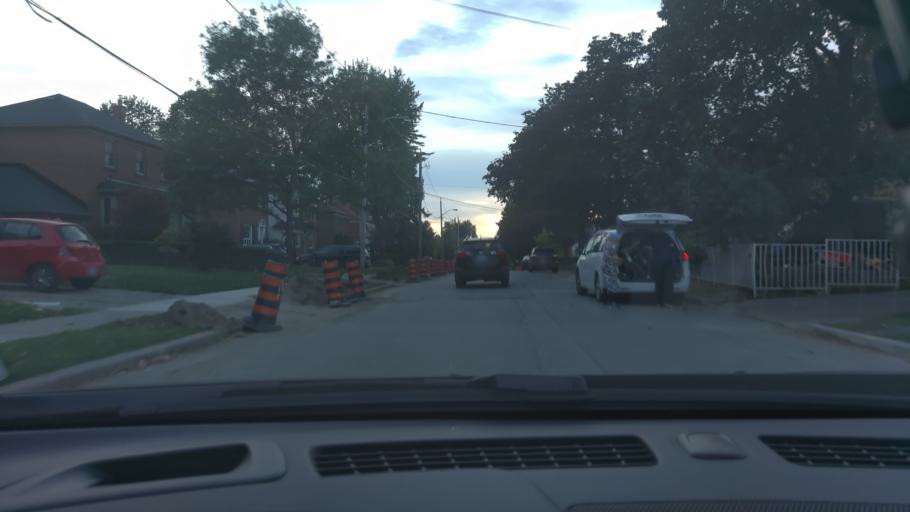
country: CA
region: Ontario
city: Toronto
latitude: 43.7175
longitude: -79.4303
